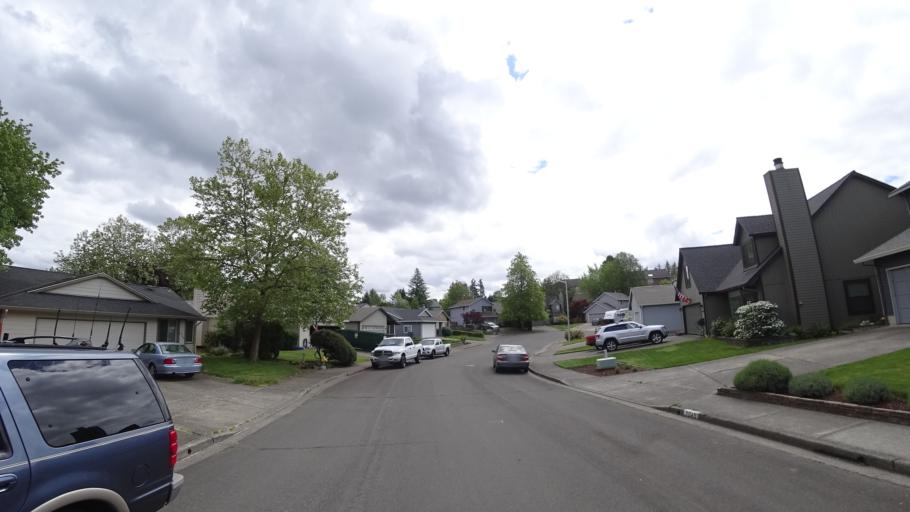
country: US
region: Oregon
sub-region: Washington County
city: Aloha
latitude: 45.4690
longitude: -122.8579
